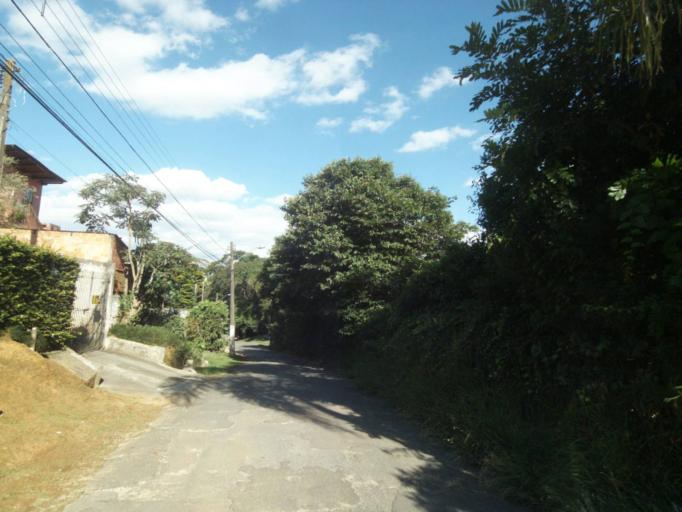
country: BR
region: Parana
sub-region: Curitiba
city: Curitiba
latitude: -25.4423
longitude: -49.3193
